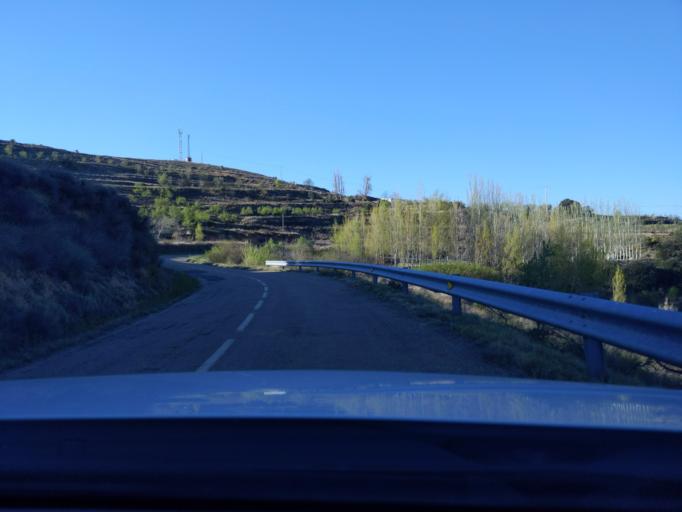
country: ES
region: La Rioja
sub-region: Provincia de La Rioja
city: Bergasillas Bajera
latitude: 42.2426
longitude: -2.1612
